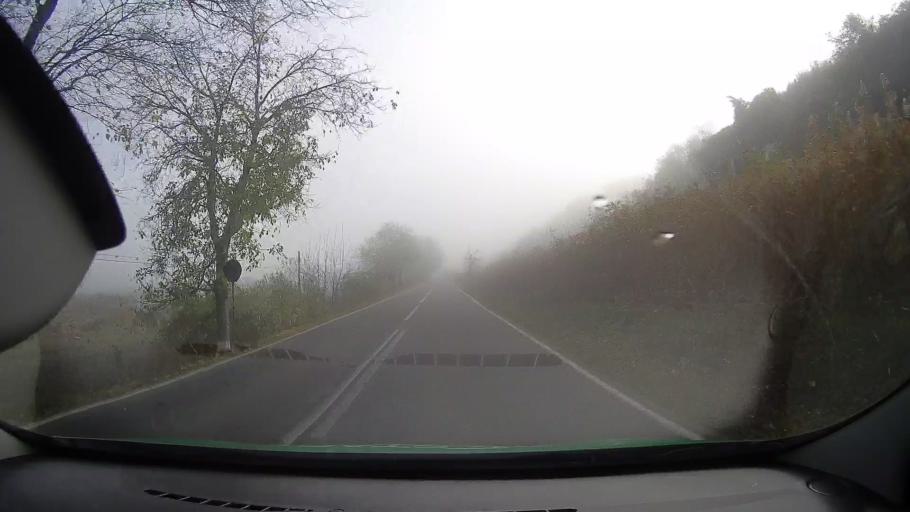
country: RO
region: Tulcea
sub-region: Comuna Nufaru
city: Malcoci
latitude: 45.1461
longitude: 28.8986
